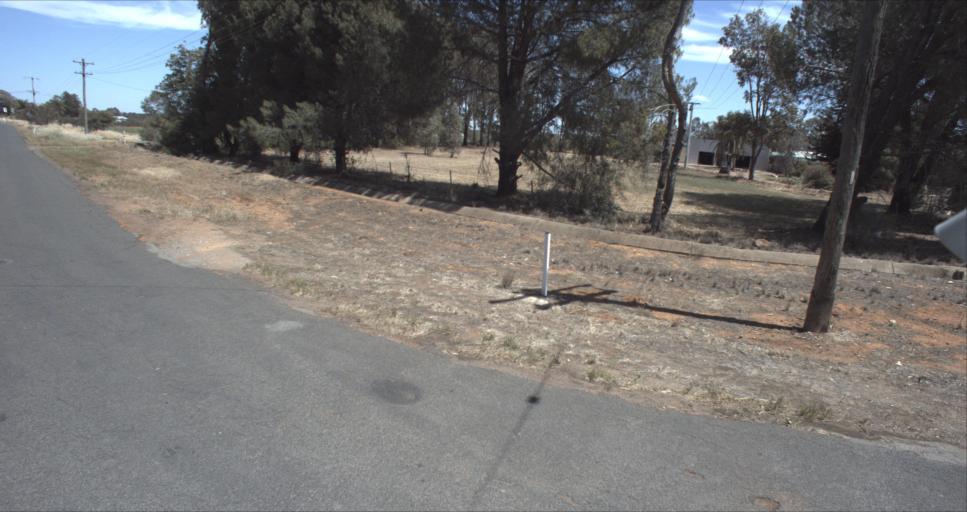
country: AU
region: New South Wales
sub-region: Leeton
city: Leeton
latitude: -34.5924
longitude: 146.4295
